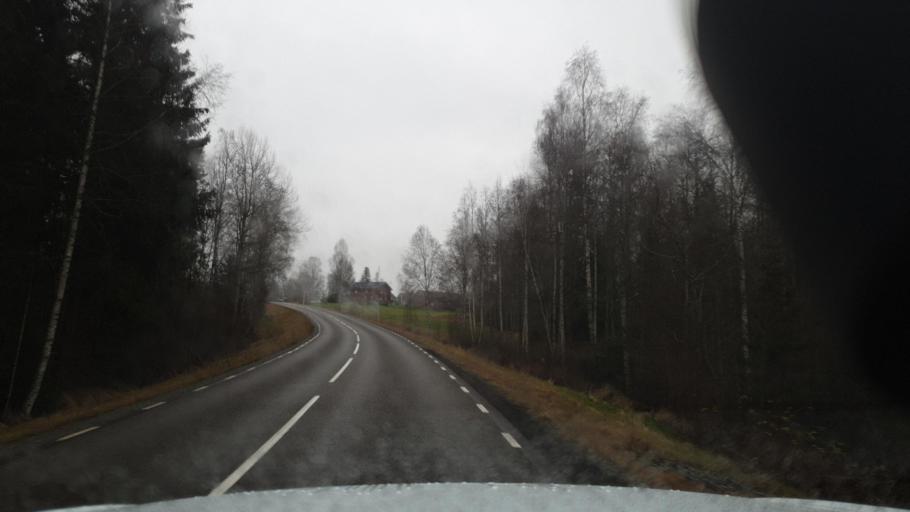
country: SE
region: Vaermland
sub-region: Eda Kommun
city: Amotfors
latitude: 59.7195
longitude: 12.4283
